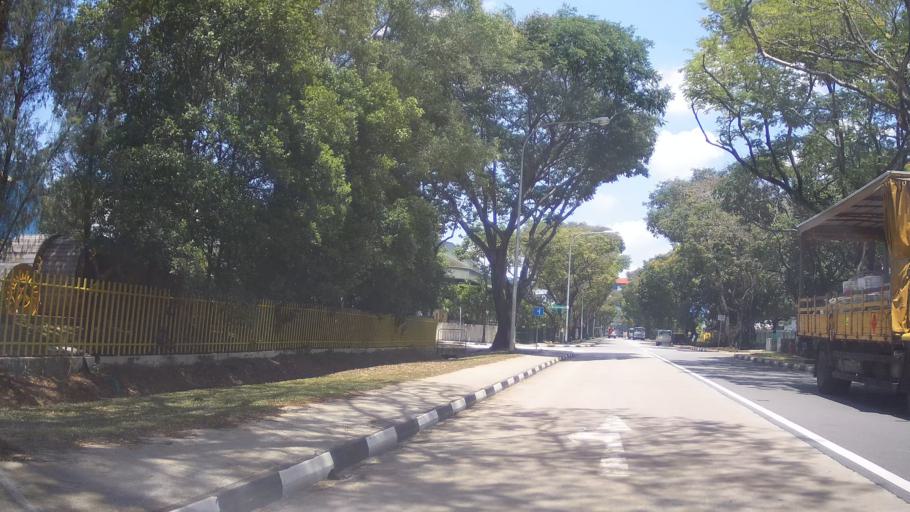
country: SG
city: Singapore
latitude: 1.3045
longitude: 103.6758
